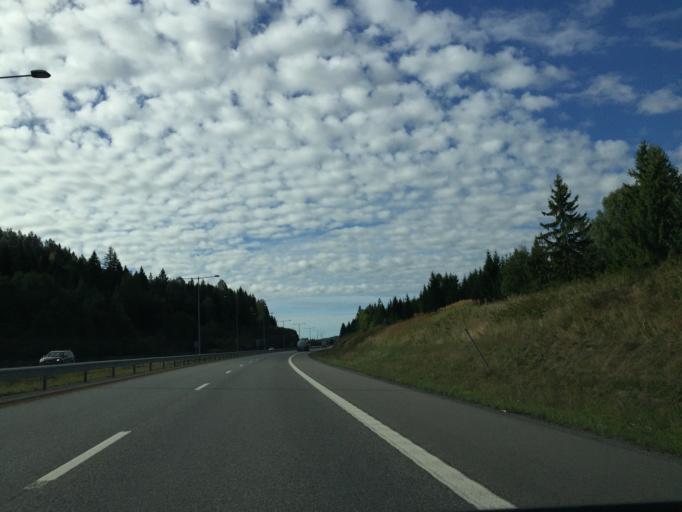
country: NO
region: Vestfold
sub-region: Sande
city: Sande
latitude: 59.5482
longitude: 10.1802
